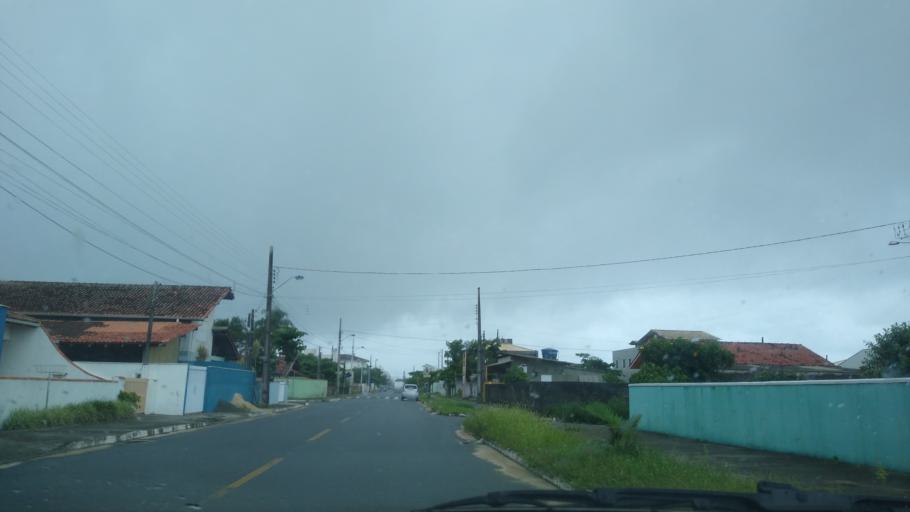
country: BR
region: Santa Catarina
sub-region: Sao Francisco Do Sul
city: Sao Francisco do Sul
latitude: -26.2330
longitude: -48.5082
